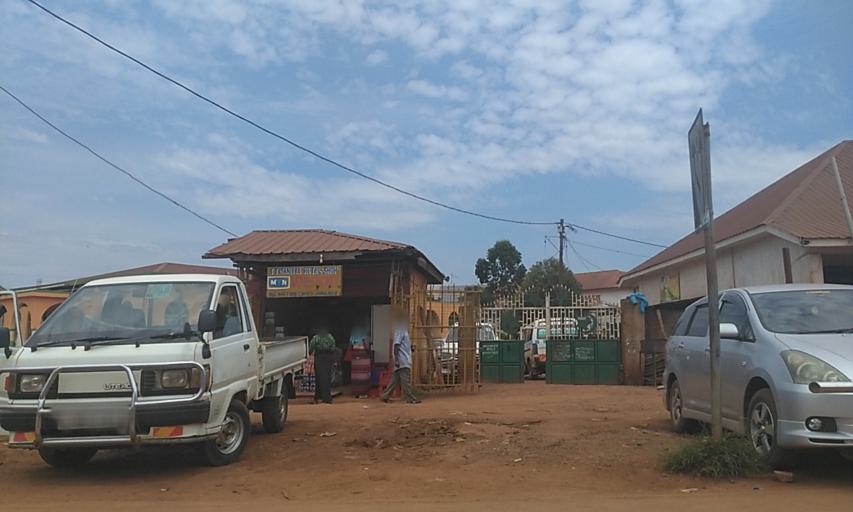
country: UG
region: Central Region
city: Kampala Central Division
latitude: 0.2990
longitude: 32.5314
